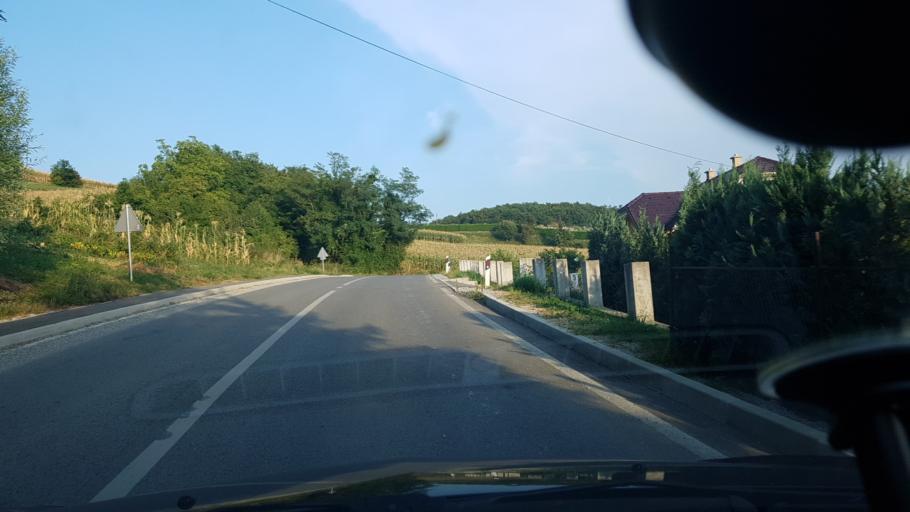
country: HR
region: Krapinsko-Zagorska
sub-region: Grad Krapina
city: Krapina
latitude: 46.1701
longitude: 15.8414
